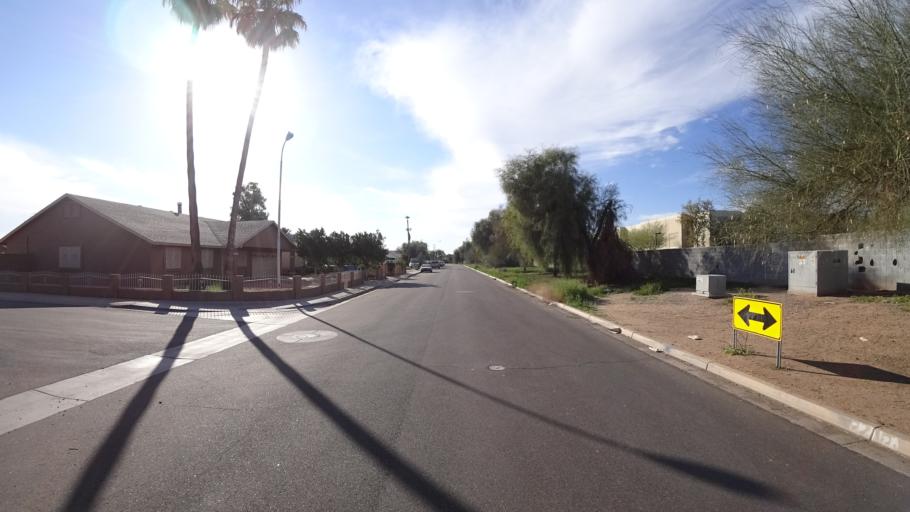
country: US
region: Arizona
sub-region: Maricopa County
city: Tolleson
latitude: 33.4587
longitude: -112.2081
